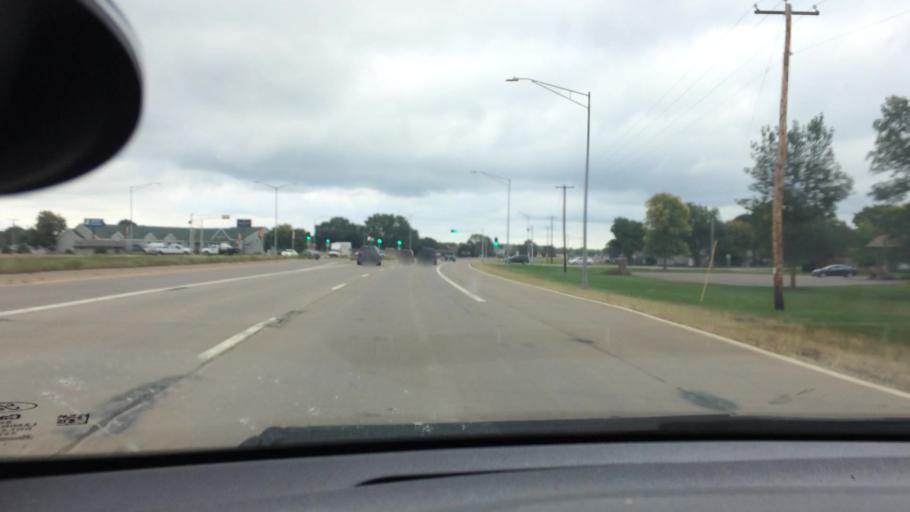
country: US
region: Wisconsin
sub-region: Chippewa County
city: Chippewa Falls
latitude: 44.9107
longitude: -91.4025
